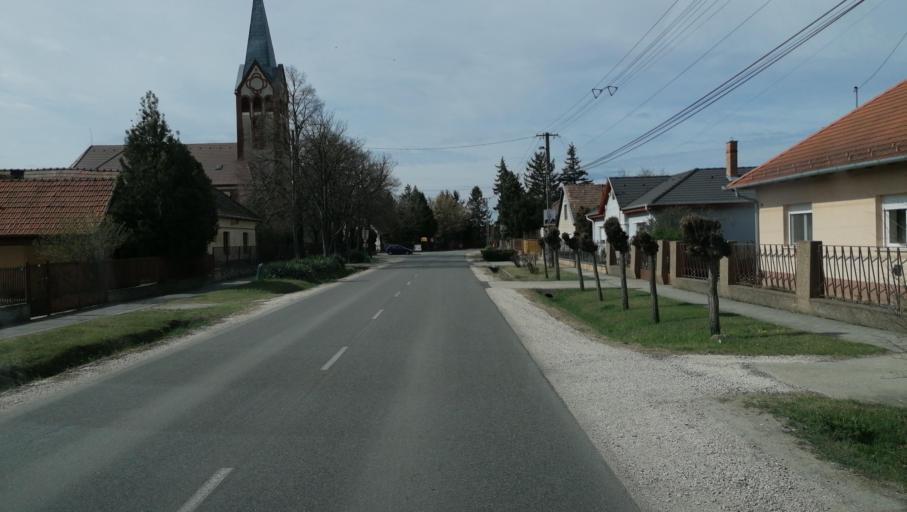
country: HU
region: Pest
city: Dabas
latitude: 47.1731
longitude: 19.3330
